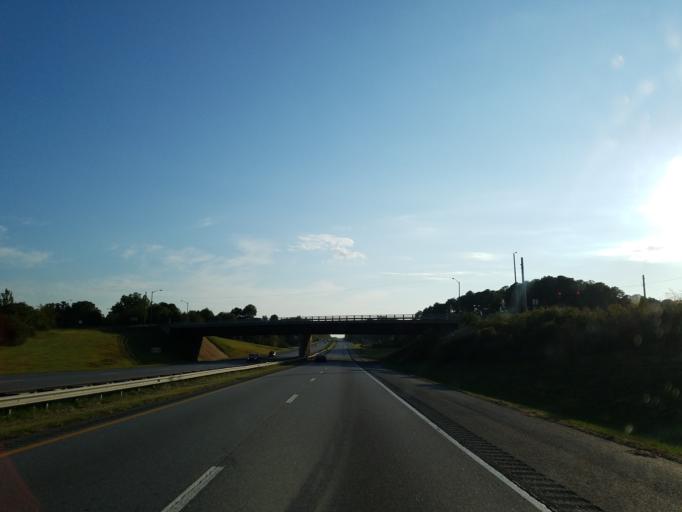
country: US
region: North Carolina
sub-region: Cleveland County
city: Kings Mountain
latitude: 35.2269
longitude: -81.3321
